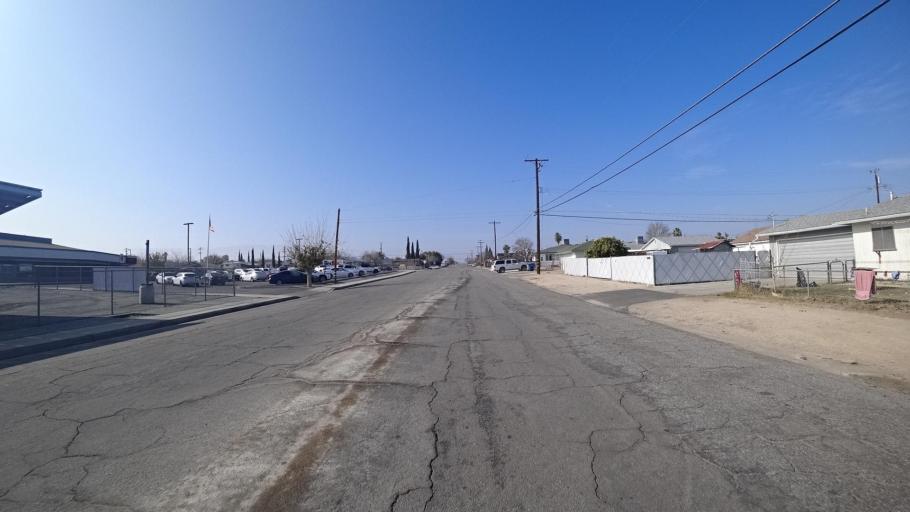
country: US
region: California
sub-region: Kern County
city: Ford City
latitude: 35.1562
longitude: -119.4591
